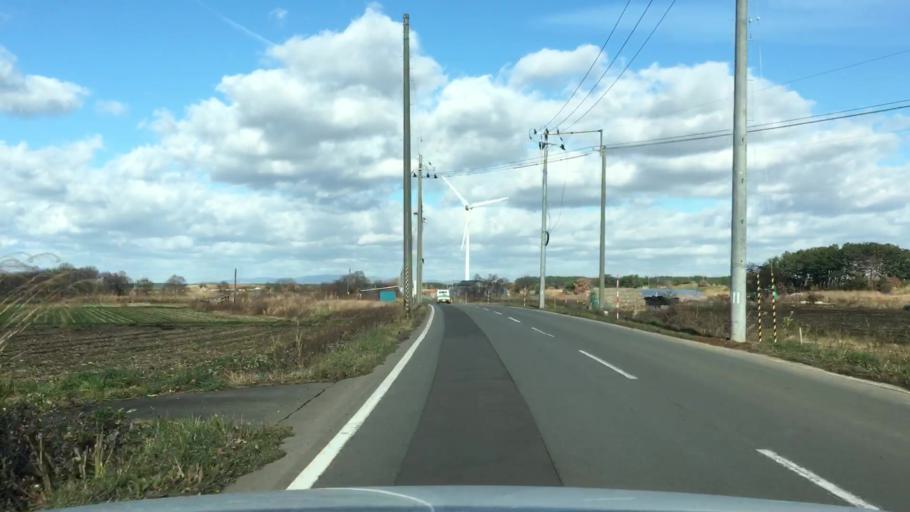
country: JP
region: Aomori
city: Shimokizukuri
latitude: 40.8565
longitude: 140.3030
